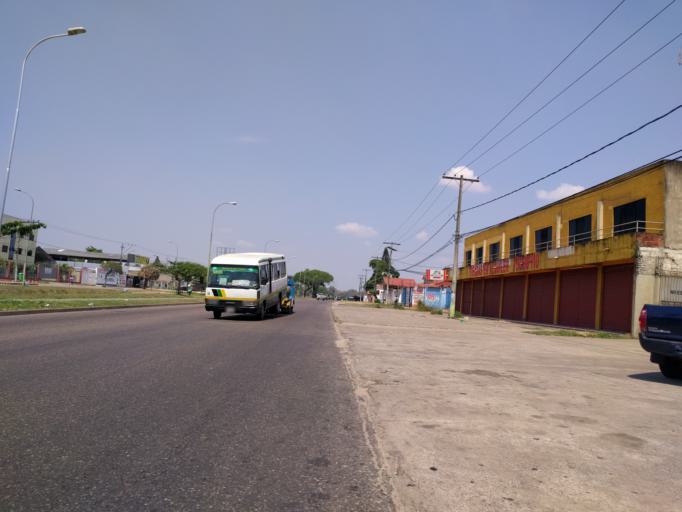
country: BO
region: Santa Cruz
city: Santa Cruz de la Sierra
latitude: -17.8074
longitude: -63.1558
